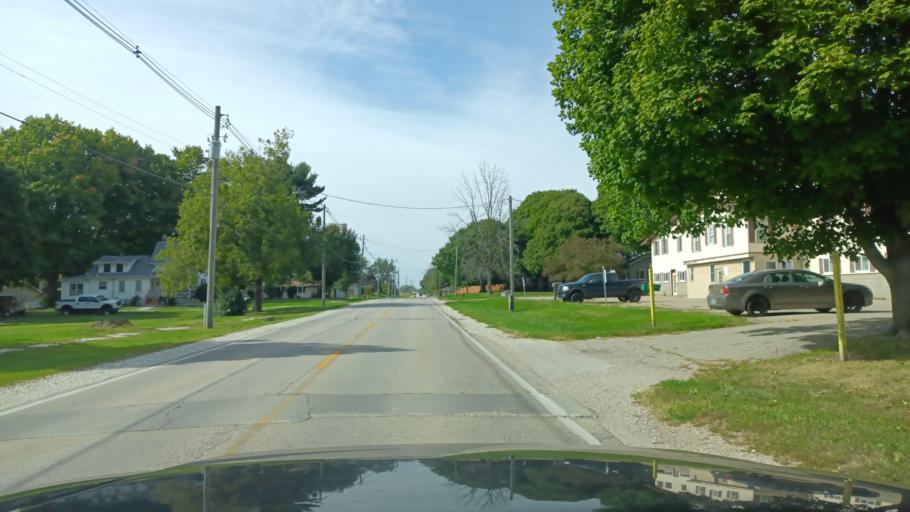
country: US
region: Illinois
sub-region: Knox County
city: Knoxville
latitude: 40.9109
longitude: -90.2947
